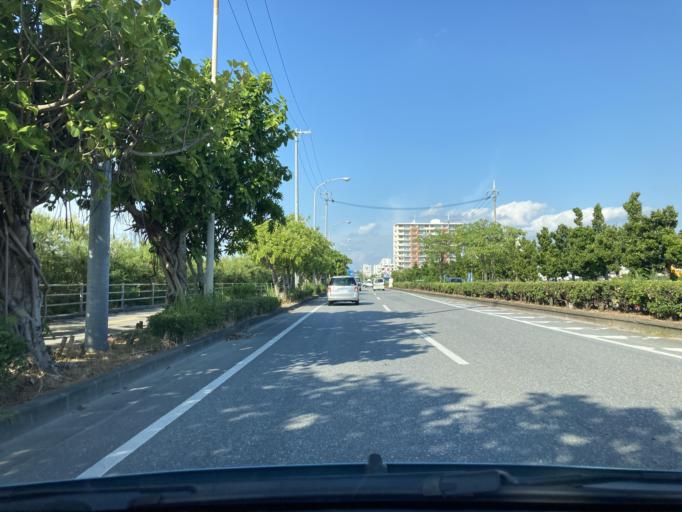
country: JP
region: Okinawa
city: Okinawa
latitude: 26.3112
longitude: 127.8281
